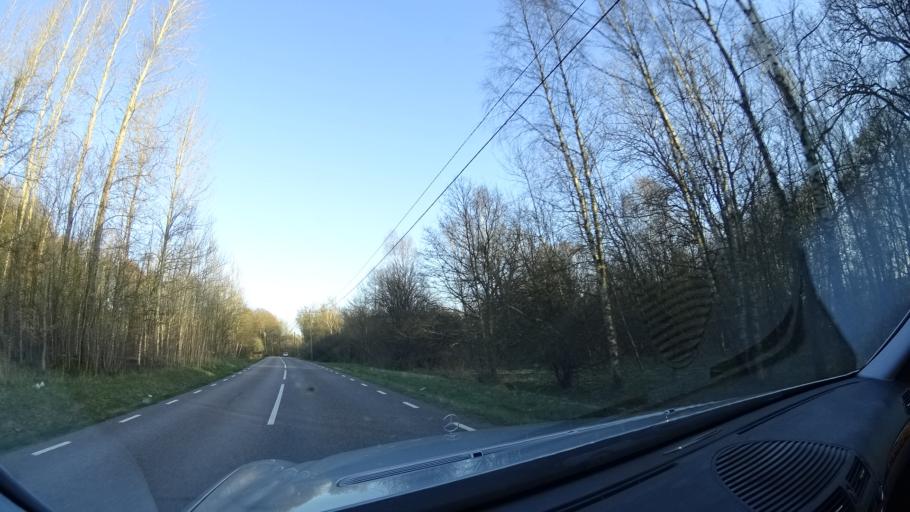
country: SE
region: Skane
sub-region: Svalovs Kommun
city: Kagerod
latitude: 55.9922
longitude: 13.0988
